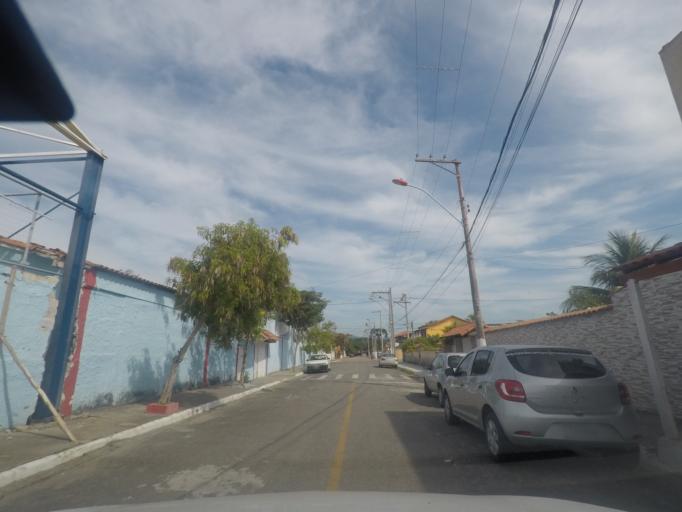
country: BR
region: Rio de Janeiro
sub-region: Marica
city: Marica
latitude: -22.9561
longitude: -42.8111
